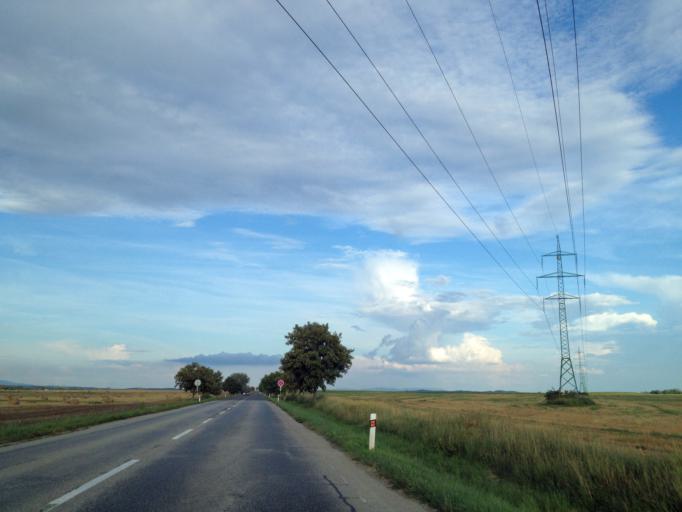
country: SK
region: Nitriansky
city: Svodin
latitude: 47.8978
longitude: 18.3717
